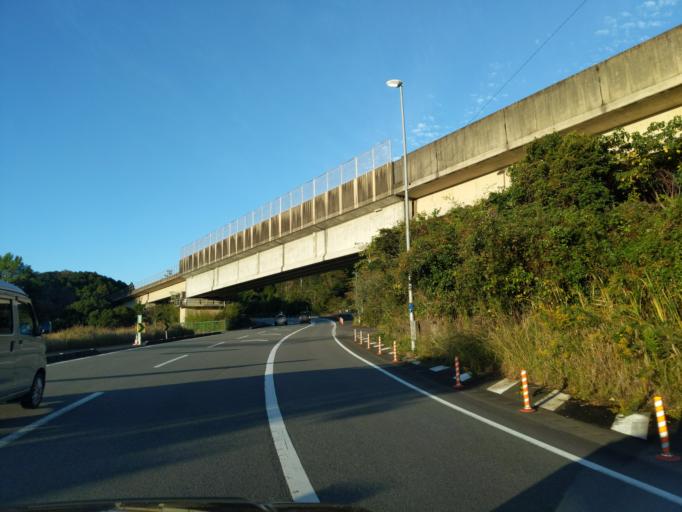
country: JP
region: Kochi
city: Muroto-misakicho
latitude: 33.5807
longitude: 134.3158
